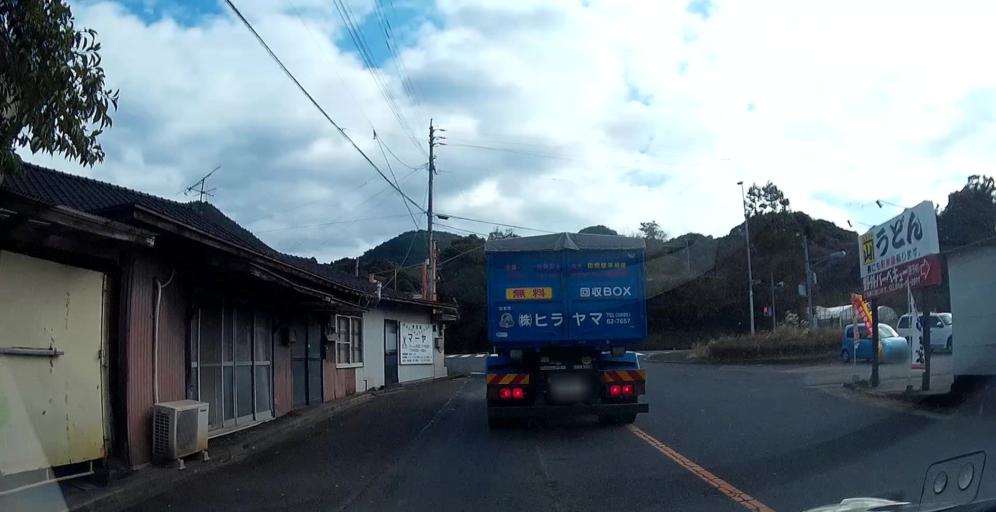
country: JP
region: Kumamoto
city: Minamata
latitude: 32.2265
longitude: 130.4379
